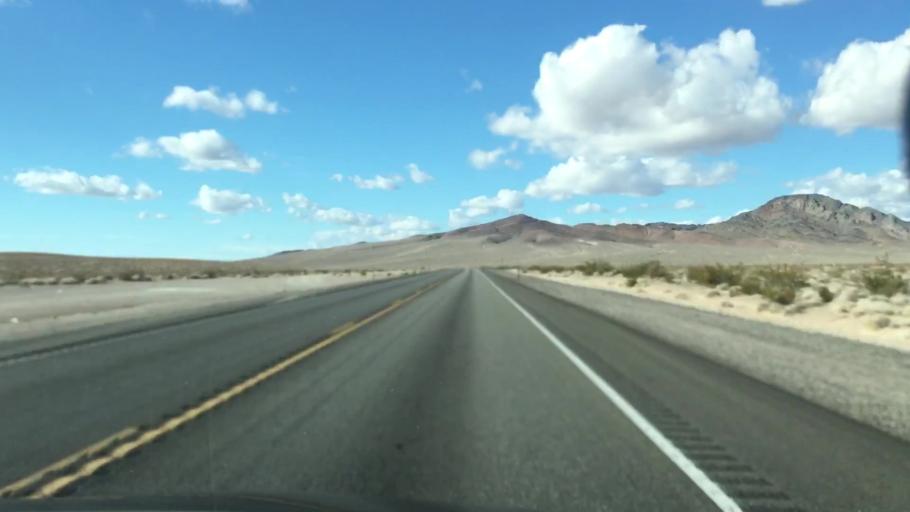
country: US
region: Nevada
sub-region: Nye County
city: Beatty
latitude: 36.6283
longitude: -116.3131
